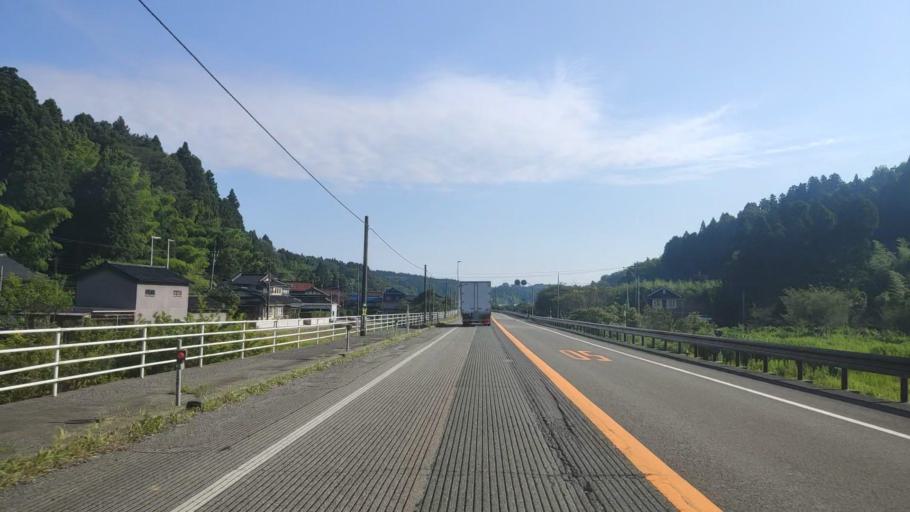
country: JP
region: Fukui
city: Maruoka
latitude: 36.2803
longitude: 136.2924
